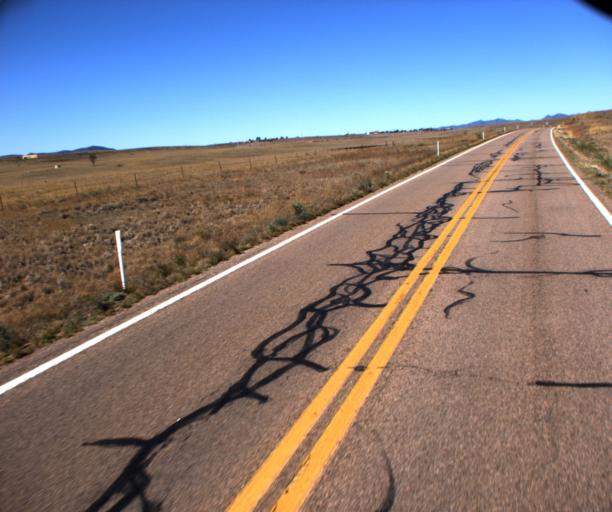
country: US
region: Arizona
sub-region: Cochise County
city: Huachuca City
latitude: 31.6837
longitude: -110.6249
